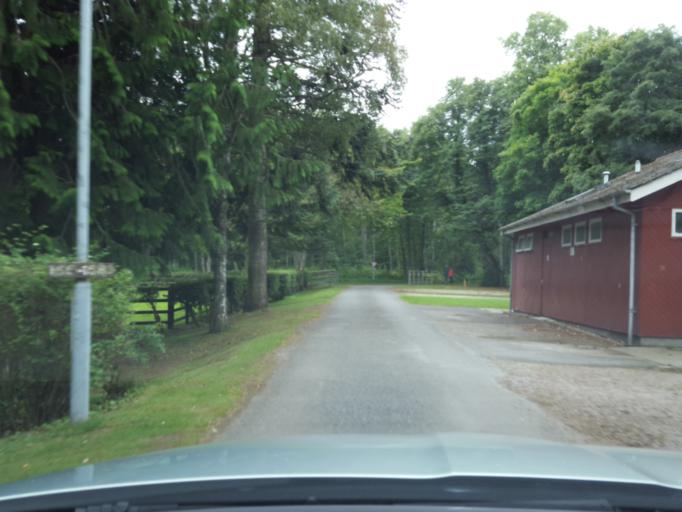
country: GB
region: Scotland
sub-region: Aberdeenshire
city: Alford
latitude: 57.2407
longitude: -2.6956
